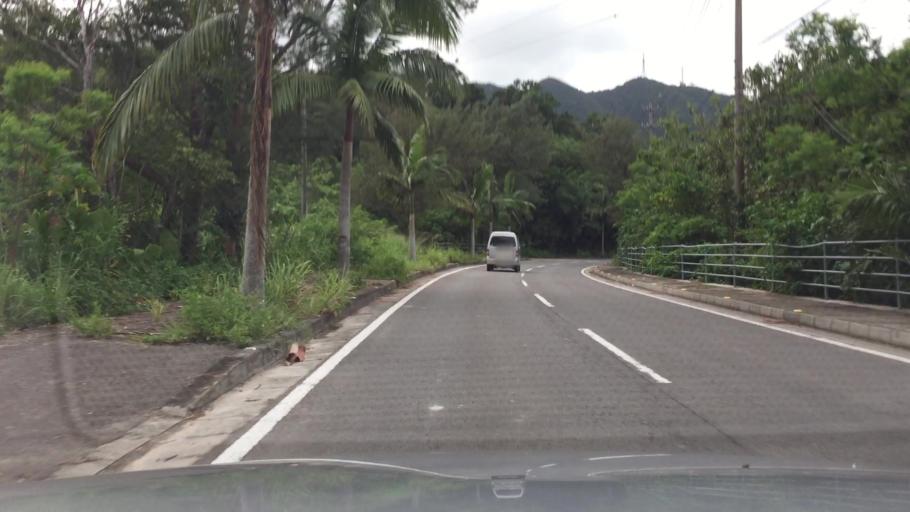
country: JP
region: Okinawa
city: Ishigaki
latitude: 24.4443
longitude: 124.1361
